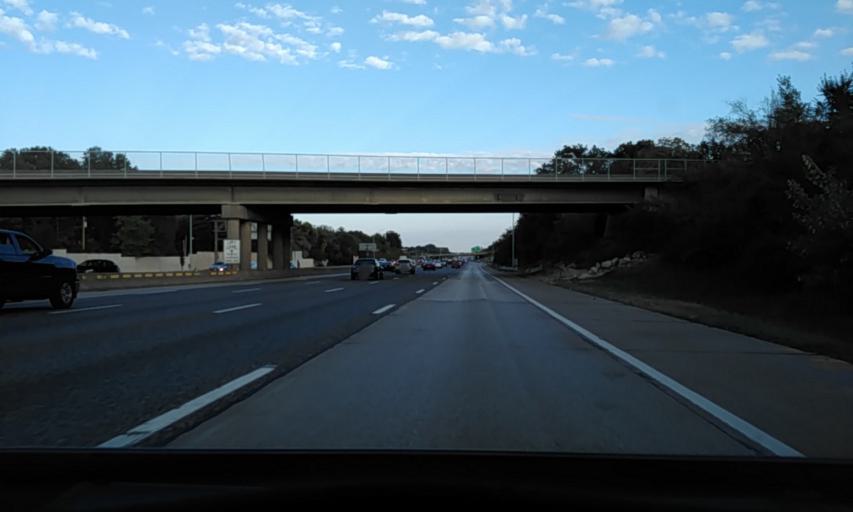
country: US
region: Missouri
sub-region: Saint Louis County
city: Sappington
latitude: 38.5155
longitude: -90.3810
